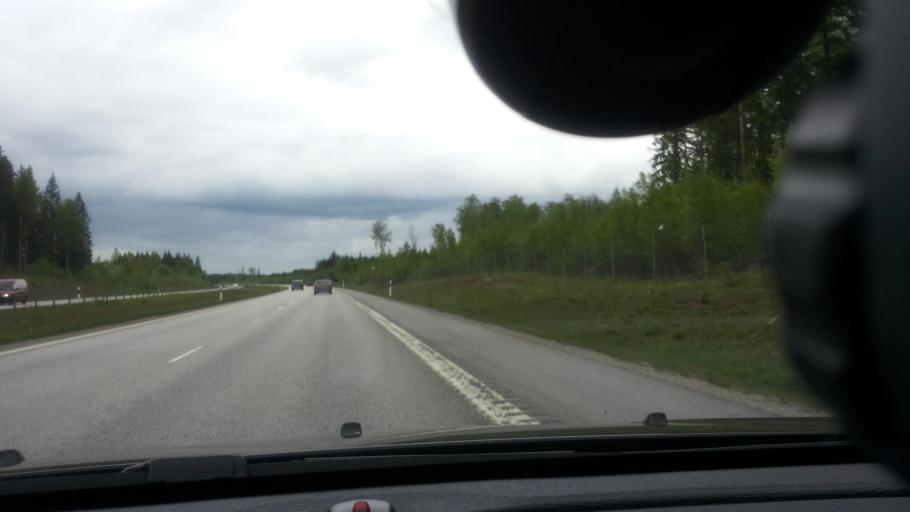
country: SE
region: Uppsala
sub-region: Tierps Kommun
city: Tierp
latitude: 60.3690
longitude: 17.4800
